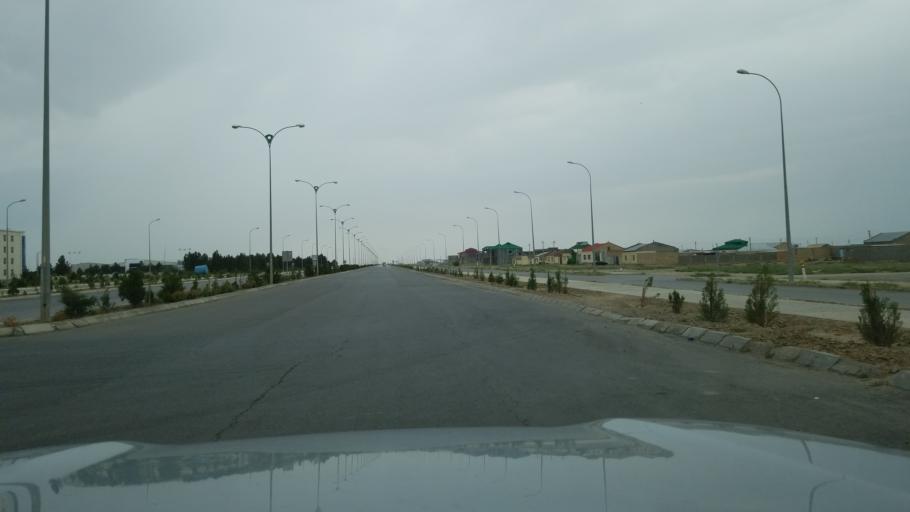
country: TM
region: Balkan
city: Serdar
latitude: 38.9998
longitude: 56.2670
